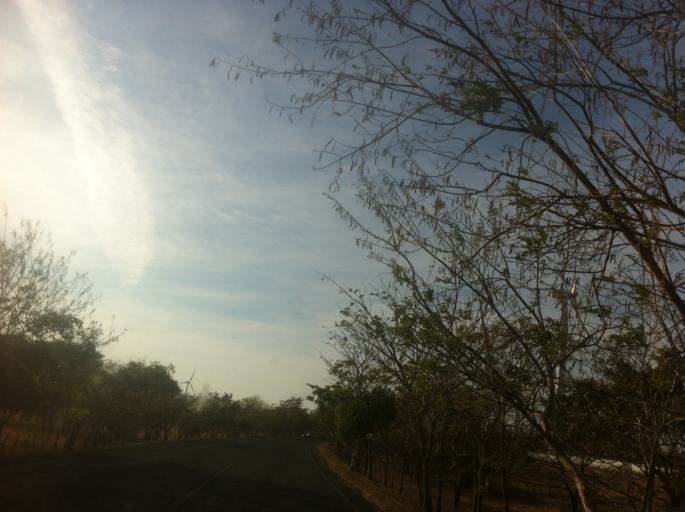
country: NI
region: Rivas
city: San Jorge
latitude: 11.3096
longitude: -85.6945
